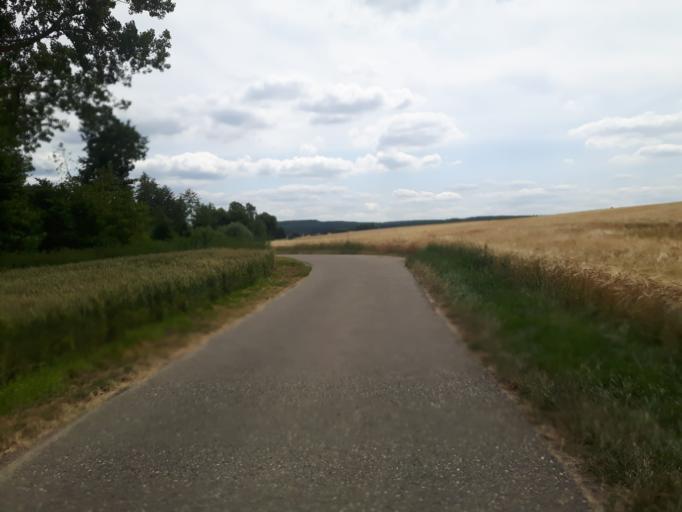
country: DE
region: Baden-Wuerttemberg
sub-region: Regierungsbezirk Stuttgart
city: Eppingen
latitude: 49.1225
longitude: 8.8895
